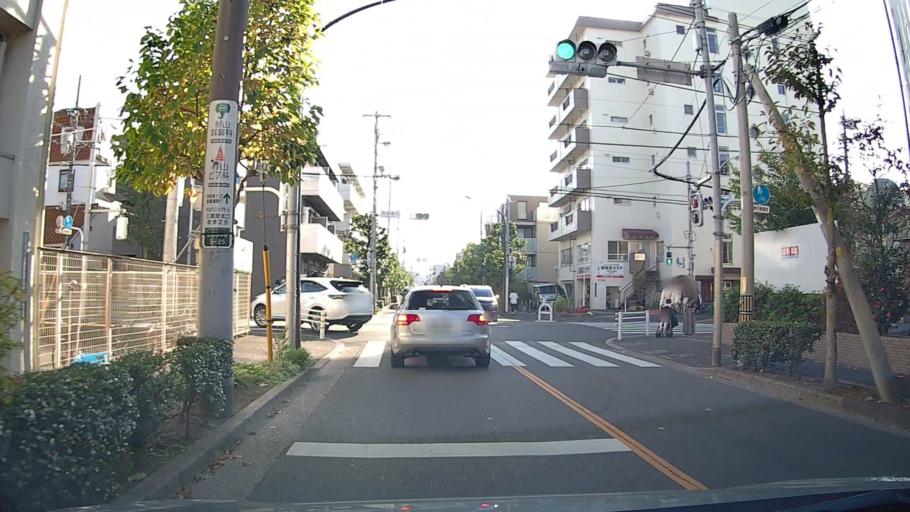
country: JP
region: Tokyo
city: Musashino
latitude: 35.7059
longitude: 139.5682
